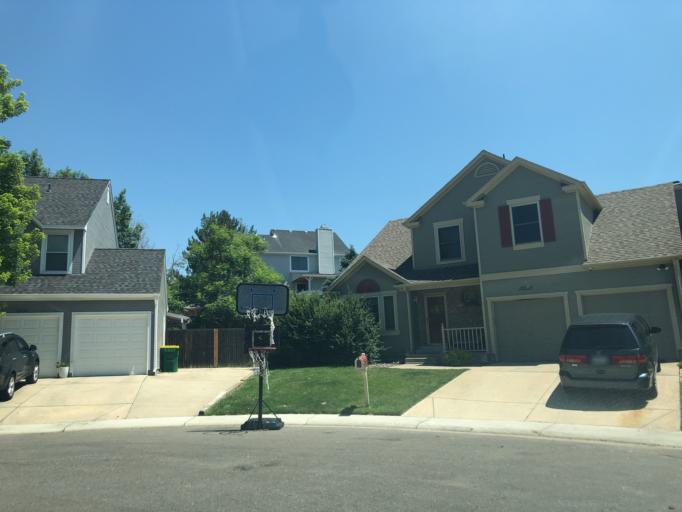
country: US
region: Colorado
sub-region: Arapahoe County
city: Dove Valley
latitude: 39.6256
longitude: -104.7753
